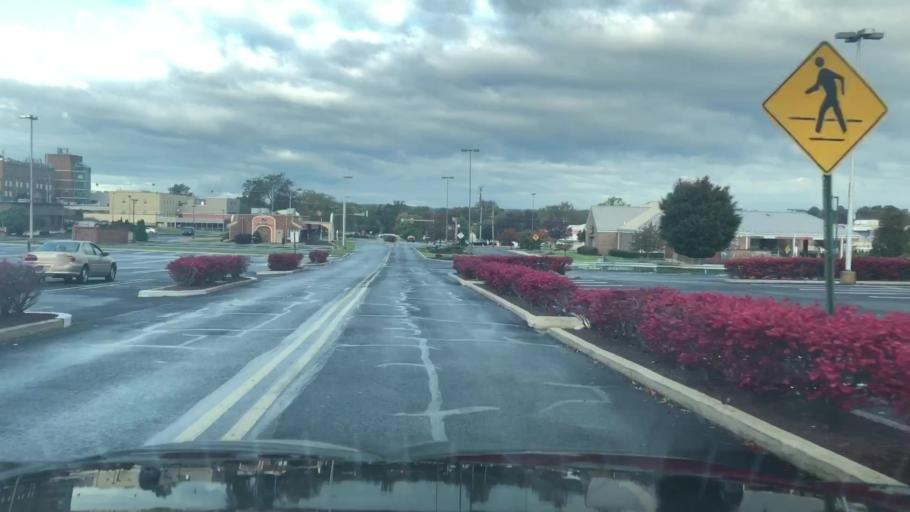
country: US
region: Pennsylvania
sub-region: Montgomery County
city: Norristown
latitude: 40.1391
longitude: -75.3122
